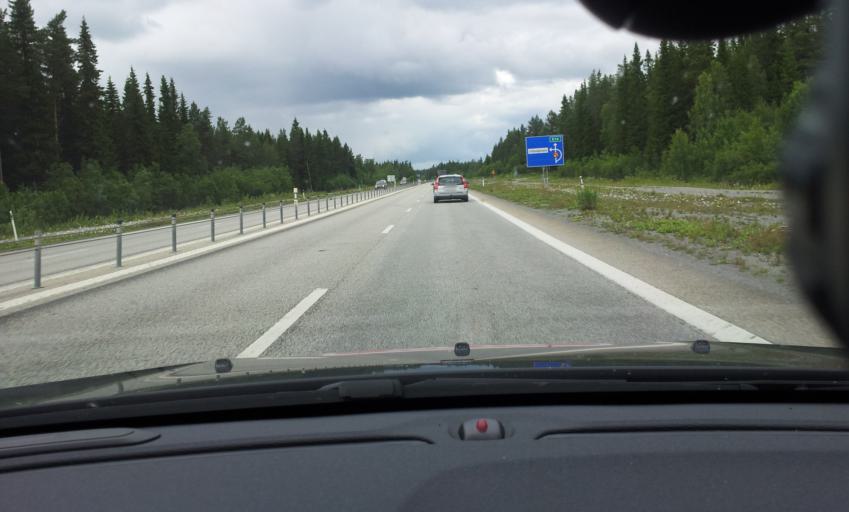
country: SE
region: Jaemtland
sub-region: OEstersunds Kommun
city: Brunflo
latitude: 63.1363
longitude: 14.7872
